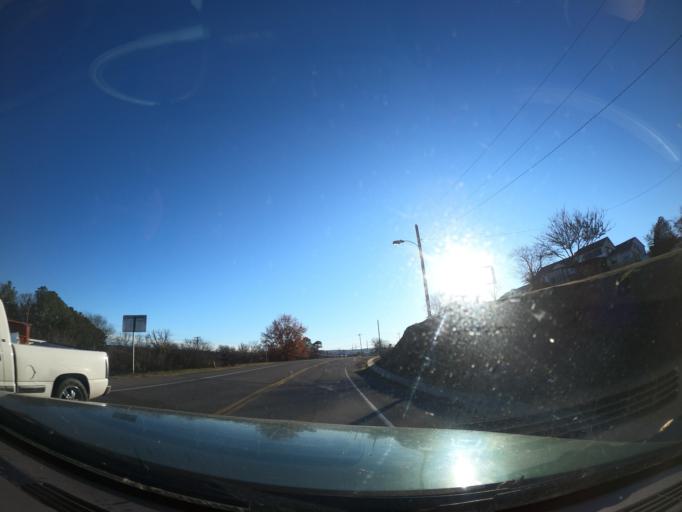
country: US
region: Oklahoma
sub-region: Latimer County
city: Wilburton
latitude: 34.9160
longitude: -95.3173
